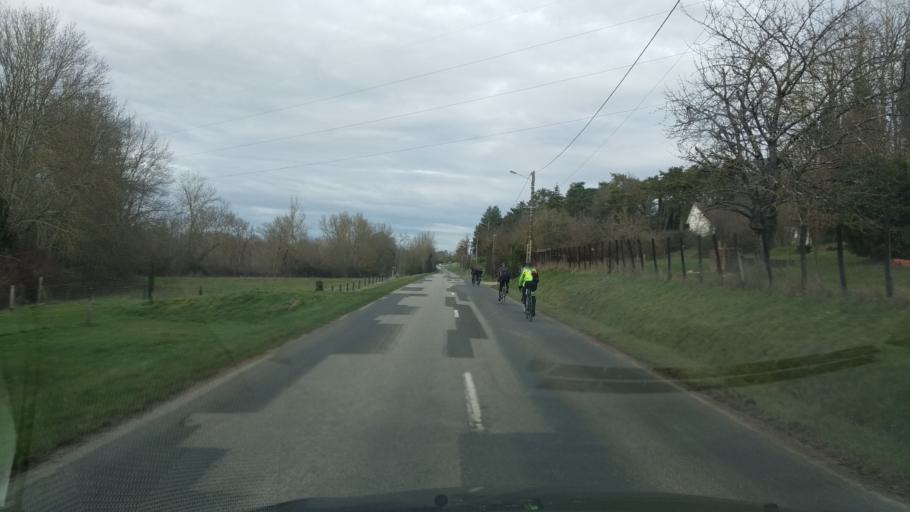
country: FR
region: Poitou-Charentes
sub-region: Departement de la Vienne
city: Chasseneuil-du-Poitou
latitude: 46.6529
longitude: 0.3884
